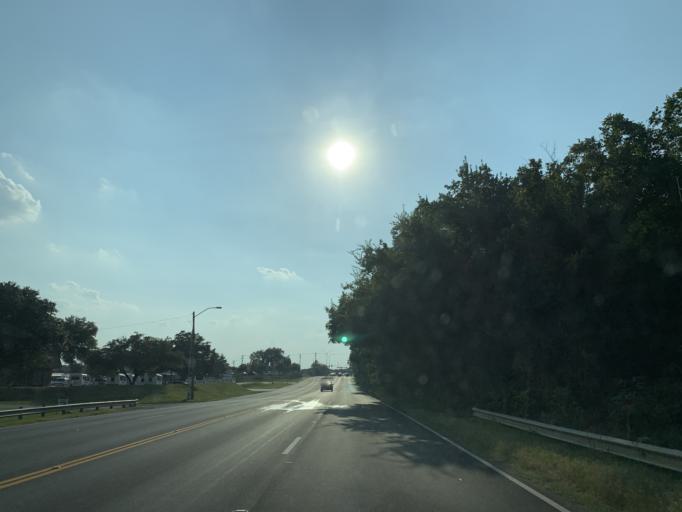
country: US
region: Texas
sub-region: Tarrant County
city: Hurst
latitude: 32.8022
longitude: -97.1795
